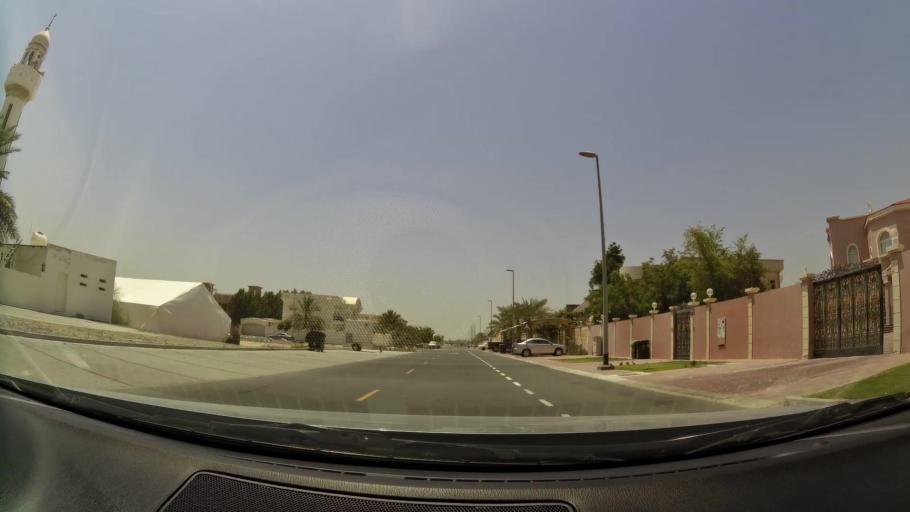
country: AE
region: Dubai
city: Dubai
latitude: 25.0838
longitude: 55.2093
